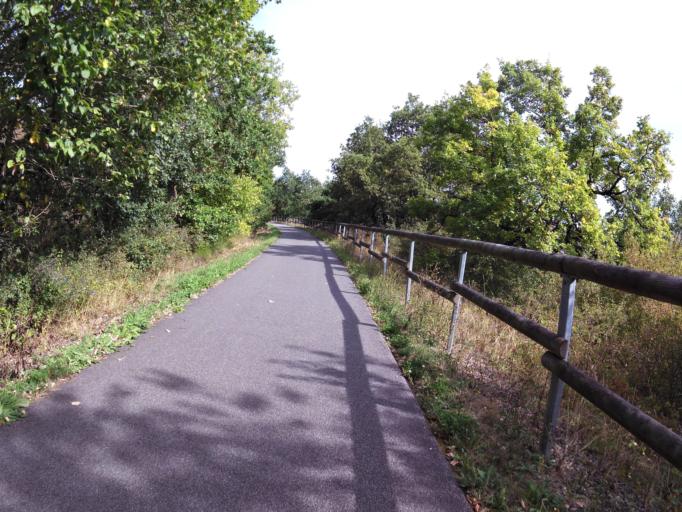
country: DE
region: Rheinland-Pfalz
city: Lunebach
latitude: 50.1410
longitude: 6.3352
